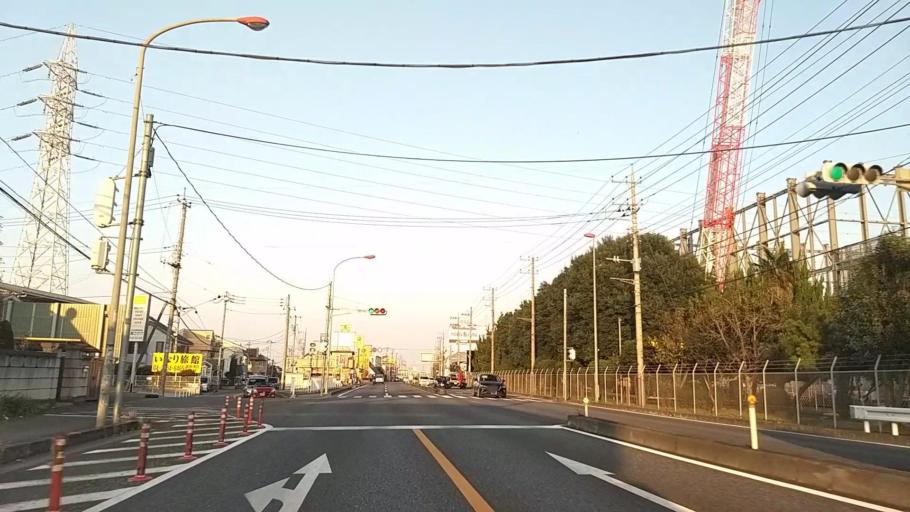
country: JP
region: Saitama
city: Sayama
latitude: 35.8802
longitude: 139.4342
